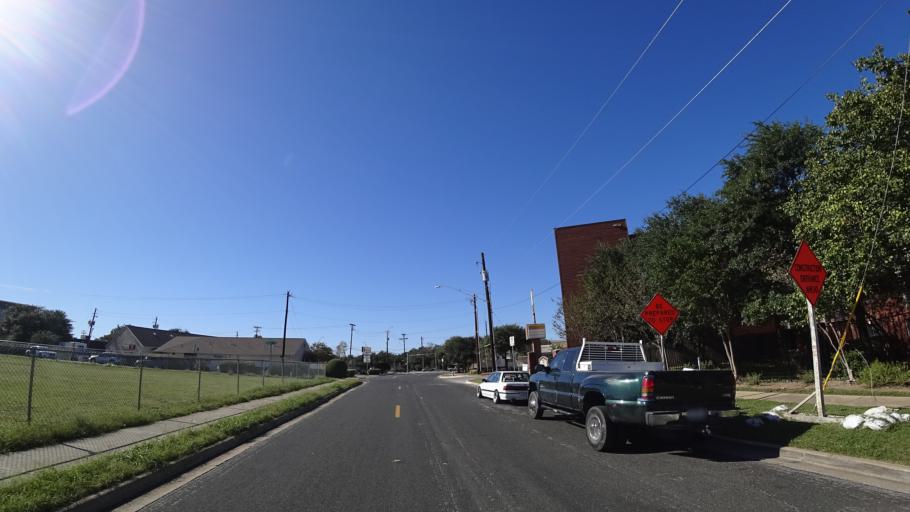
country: US
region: Texas
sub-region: Travis County
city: Rollingwood
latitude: 30.2380
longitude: -97.7882
